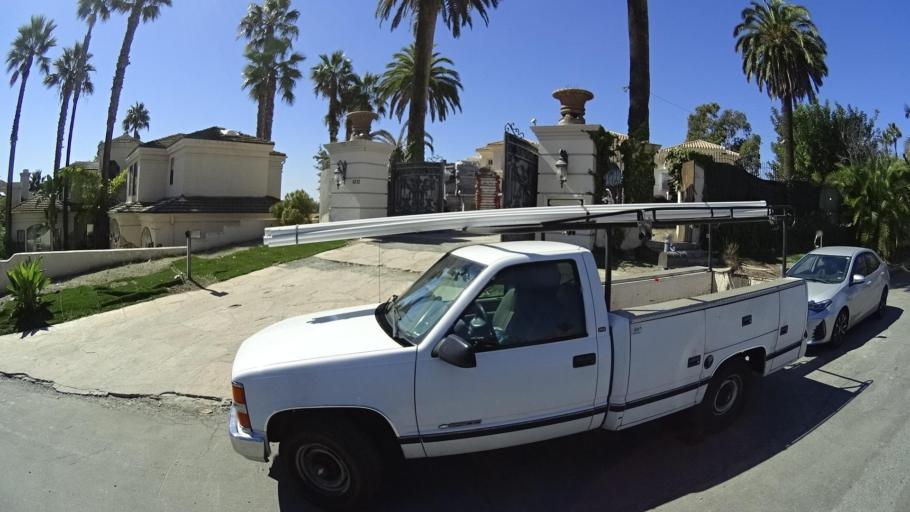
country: US
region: California
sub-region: San Diego County
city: Bonita
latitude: 32.6607
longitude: -117.0137
